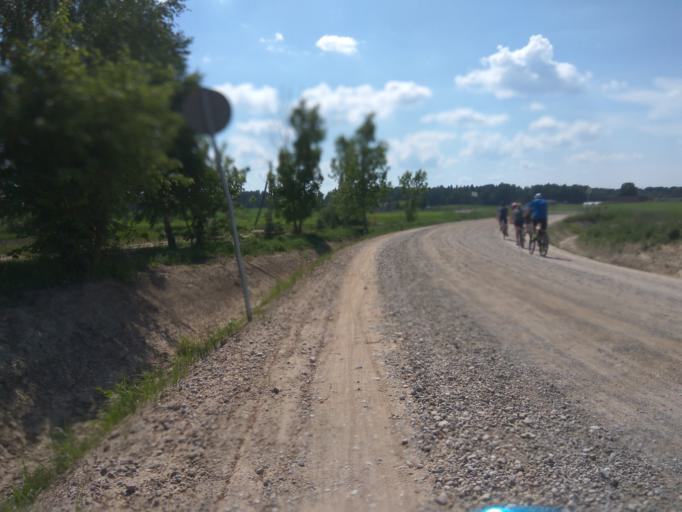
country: LV
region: Kuldigas Rajons
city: Kuldiga
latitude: 56.9477
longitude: 21.9754
